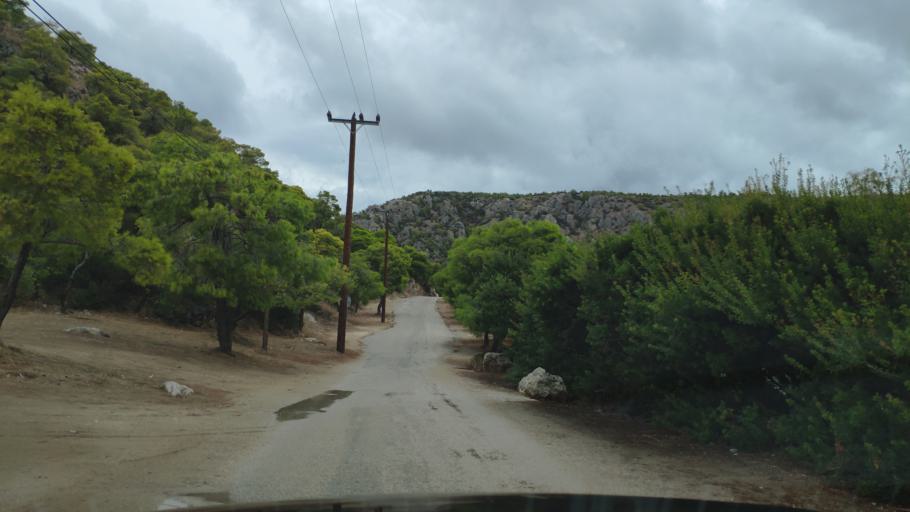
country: GR
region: Peloponnese
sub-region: Nomos Korinthias
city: Perachora
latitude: 38.0283
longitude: 22.8718
